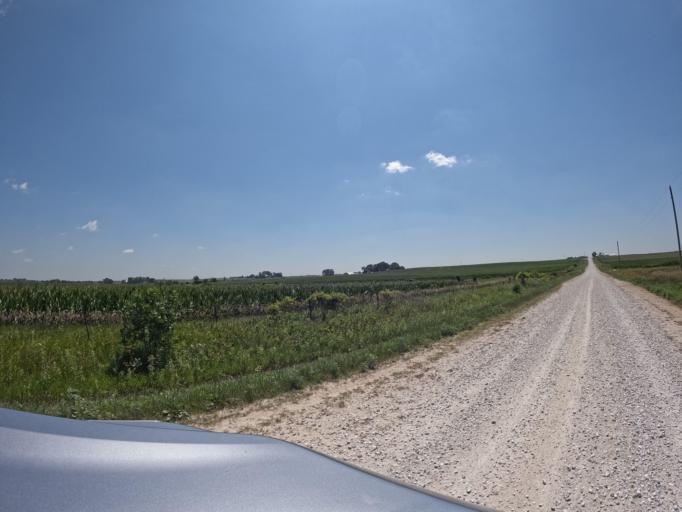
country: US
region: Iowa
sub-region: Keokuk County
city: Sigourney
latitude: 41.2917
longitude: -92.2190
